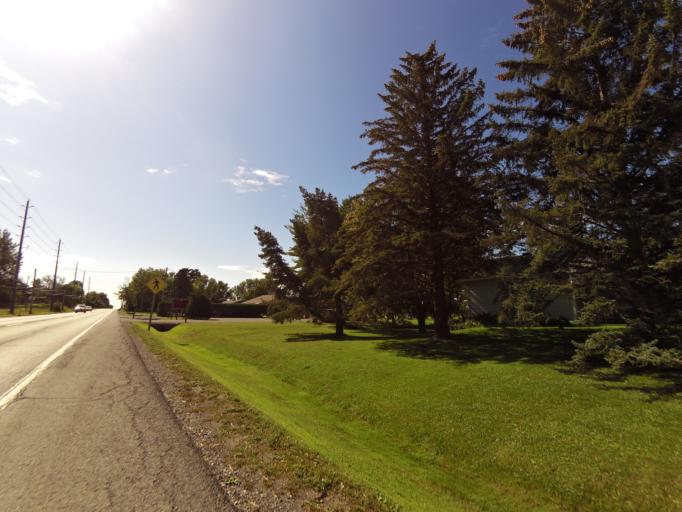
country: CA
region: Ontario
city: Bells Corners
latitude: 45.2758
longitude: -75.8344
